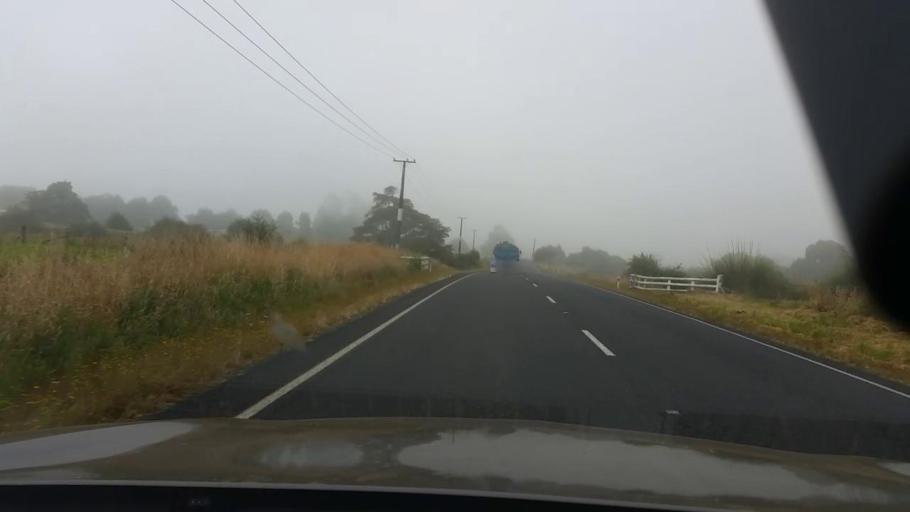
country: NZ
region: Waikato
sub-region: Hamilton City
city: Hamilton
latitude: -37.6432
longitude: 175.2952
